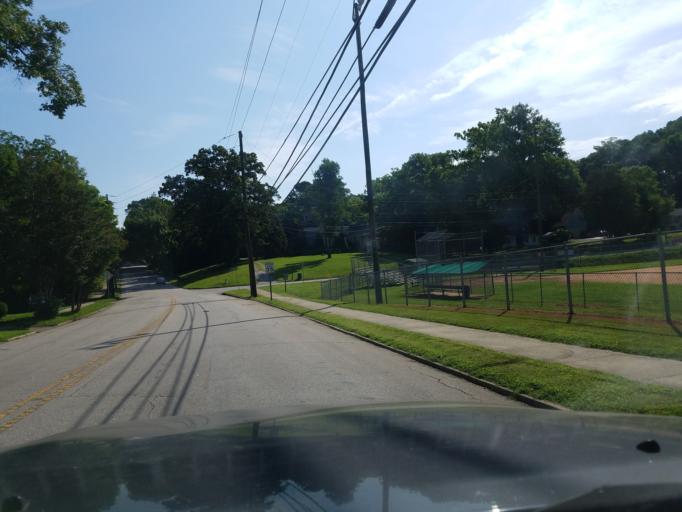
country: US
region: North Carolina
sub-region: Granville County
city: Oxford
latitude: 36.3139
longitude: -78.5842
